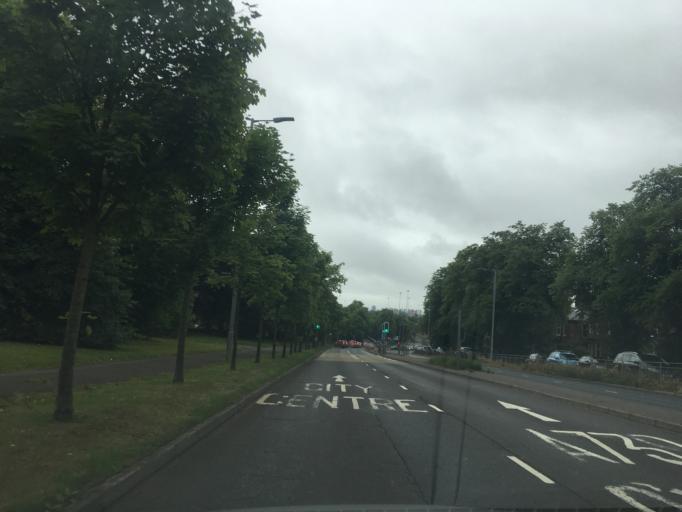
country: GB
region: Scotland
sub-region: East Dunbartonshire
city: Bearsden
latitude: 55.8784
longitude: -4.3263
